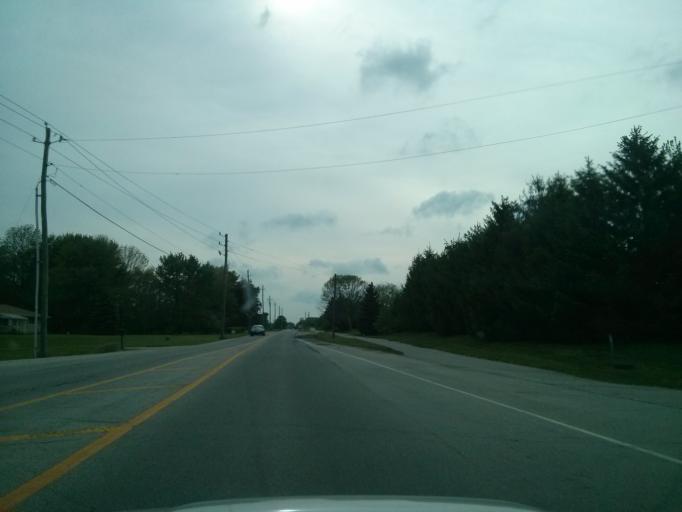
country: US
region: Indiana
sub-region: Boone County
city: Zionsville
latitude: 39.9557
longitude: -86.2039
